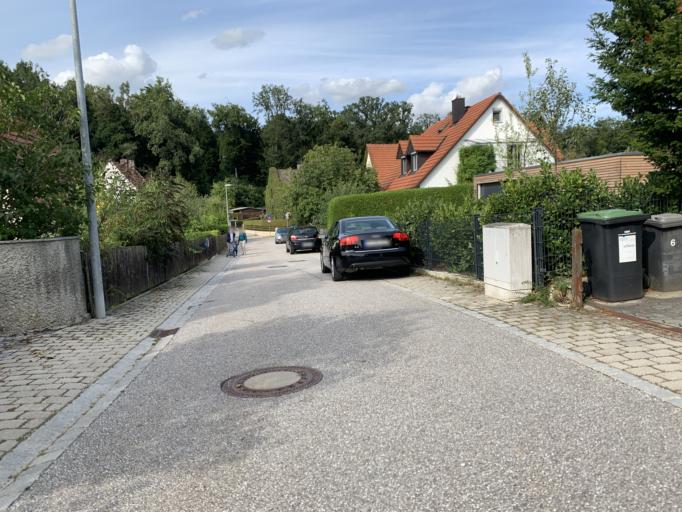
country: DE
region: Bavaria
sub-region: Upper Bavaria
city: Freising
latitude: 48.4144
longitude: 11.7316
